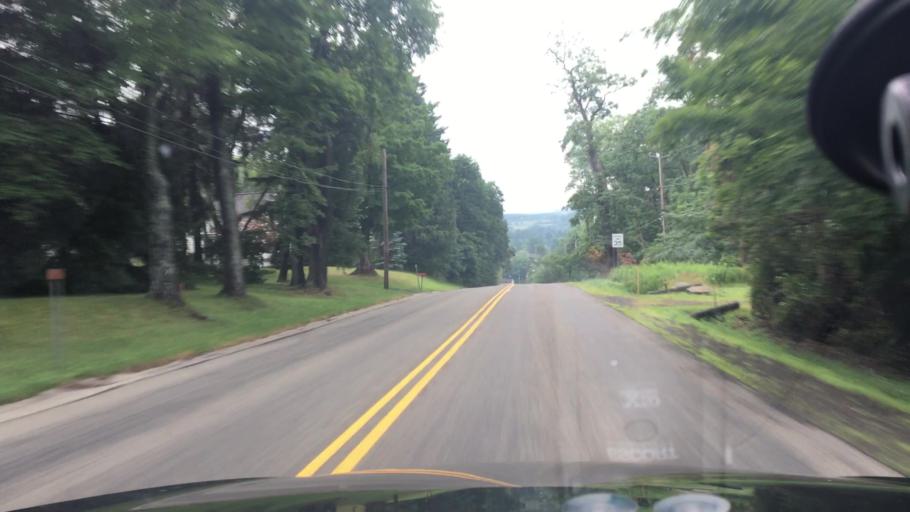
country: US
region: New York
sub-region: Chautauqua County
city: Lakewood
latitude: 42.1002
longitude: -79.3781
